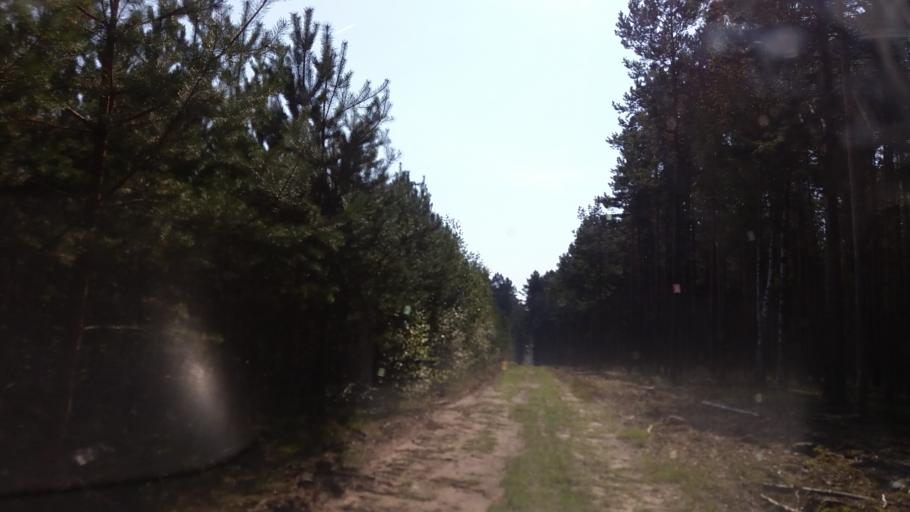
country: PL
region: West Pomeranian Voivodeship
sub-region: Powiat drawski
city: Kalisz Pomorski
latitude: 53.1866
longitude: 15.9584
